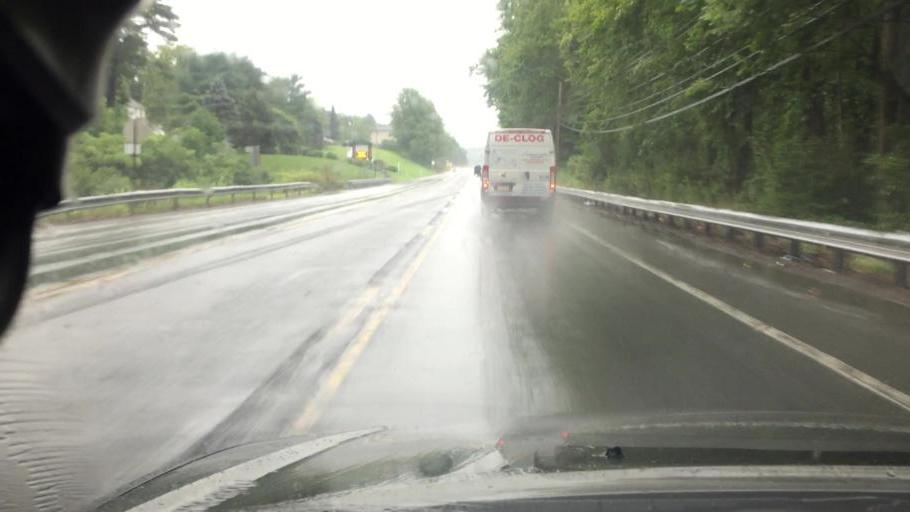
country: US
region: Pennsylvania
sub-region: Monroe County
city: Tannersville
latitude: 41.0281
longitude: -75.3001
